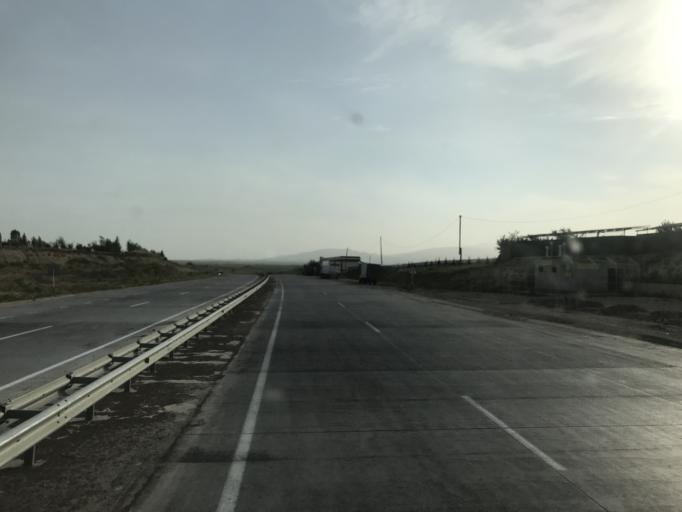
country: UZ
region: Toshkent
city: Qibray
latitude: 41.5271
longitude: 69.4007
